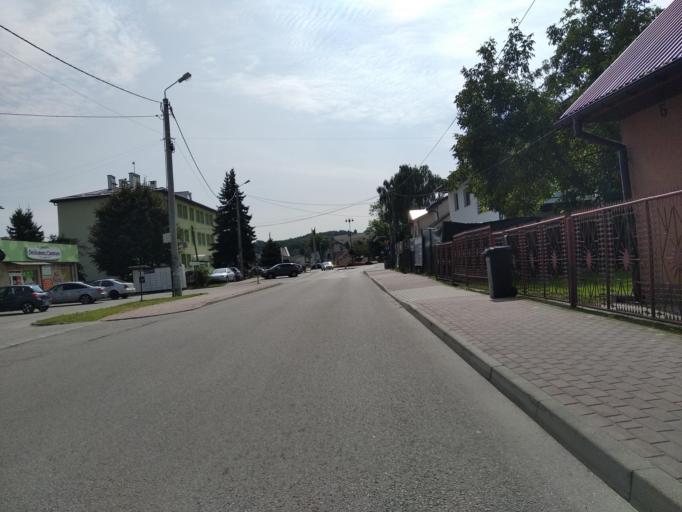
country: PL
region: Subcarpathian Voivodeship
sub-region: Powiat ropczycko-sedziszowski
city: Ropczyce
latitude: 50.0549
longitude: 21.6173
